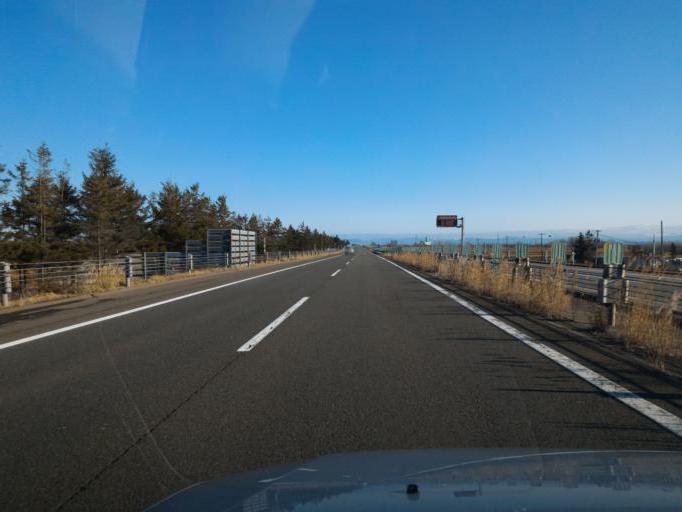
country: JP
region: Hokkaido
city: Ebetsu
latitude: 43.1078
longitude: 141.6058
